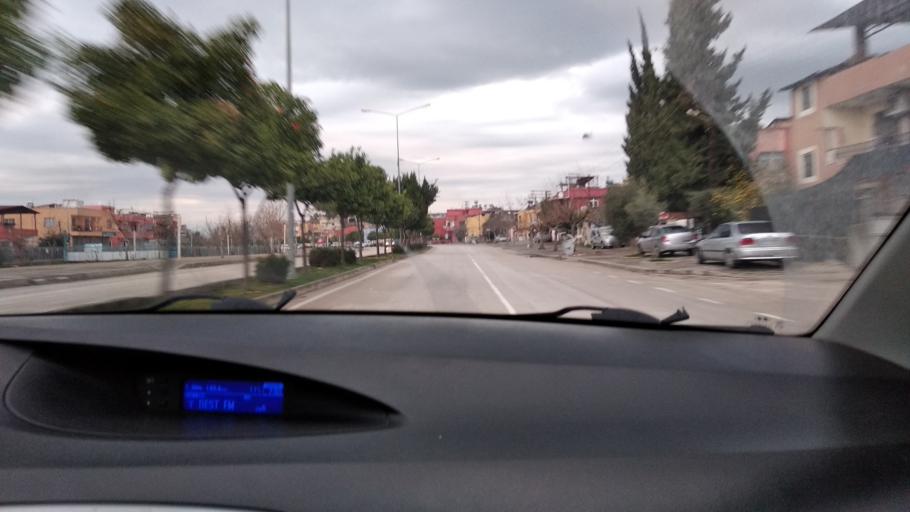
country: TR
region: Adana
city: Yuregir
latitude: 37.0133
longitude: 35.3870
